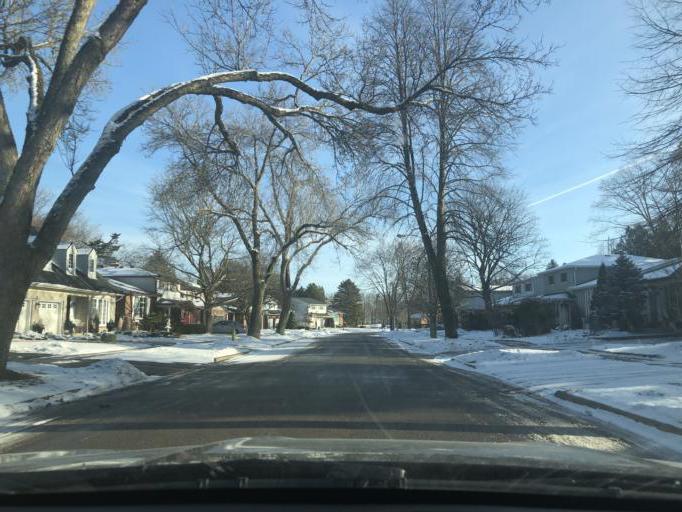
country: CA
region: Ontario
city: Scarborough
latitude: 43.7729
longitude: -79.1465
